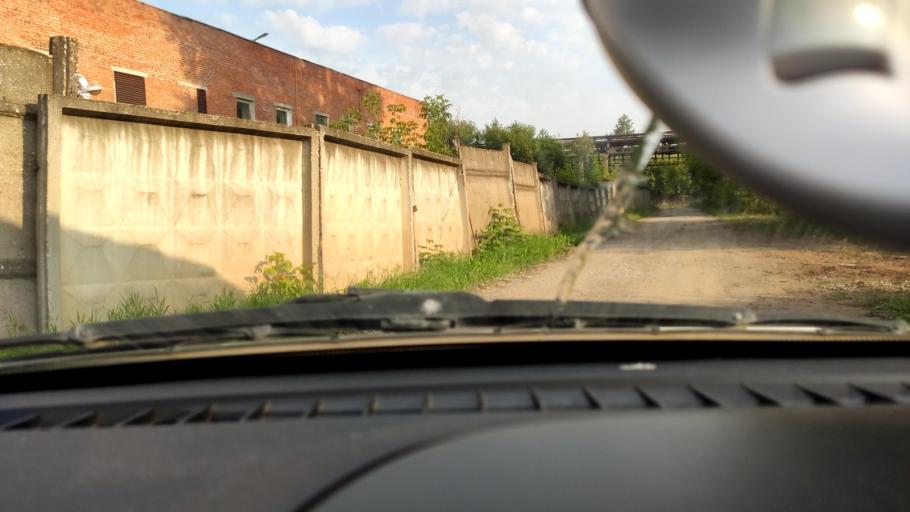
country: RU
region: Perm
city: Kondratovo
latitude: 58.0102
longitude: 56.1718
